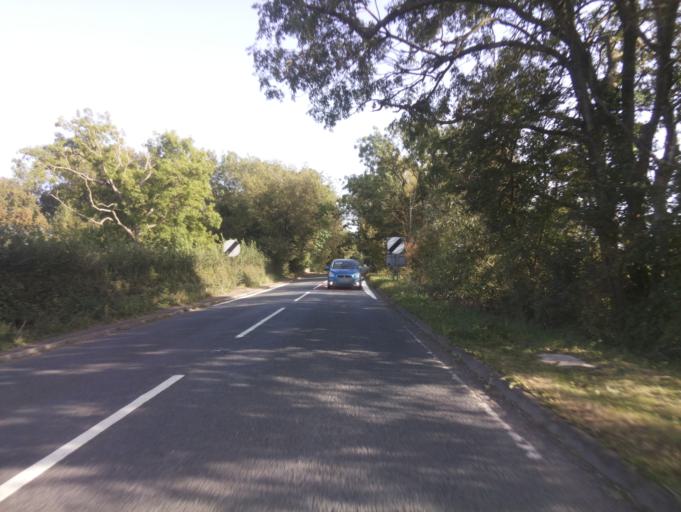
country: GB
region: England
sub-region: Gloucestershire
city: Tewkesbury
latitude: 51.9531
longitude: -2.2356
